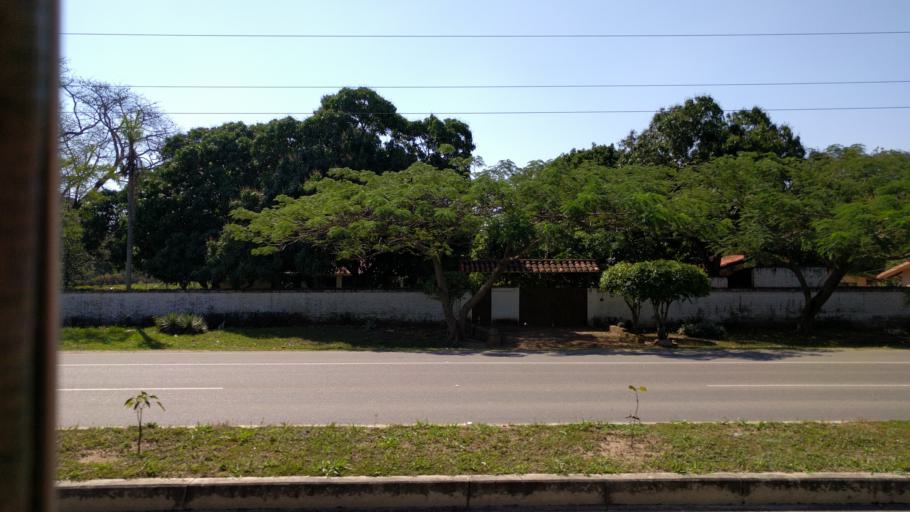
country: BO
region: Santa Cruz
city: Cotoca
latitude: -17.7577
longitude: -63.0072
